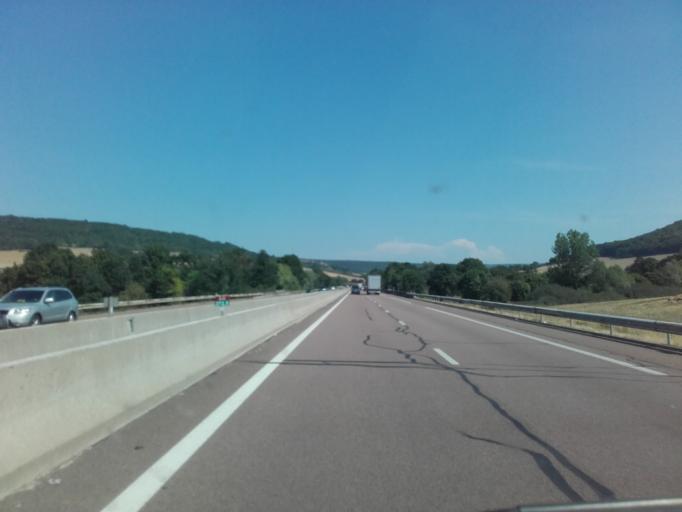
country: FR
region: Bourgogne
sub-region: Departement de la Cote-d'Or
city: Pouilly-en-Auxois
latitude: 47.2060
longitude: 4.6328
